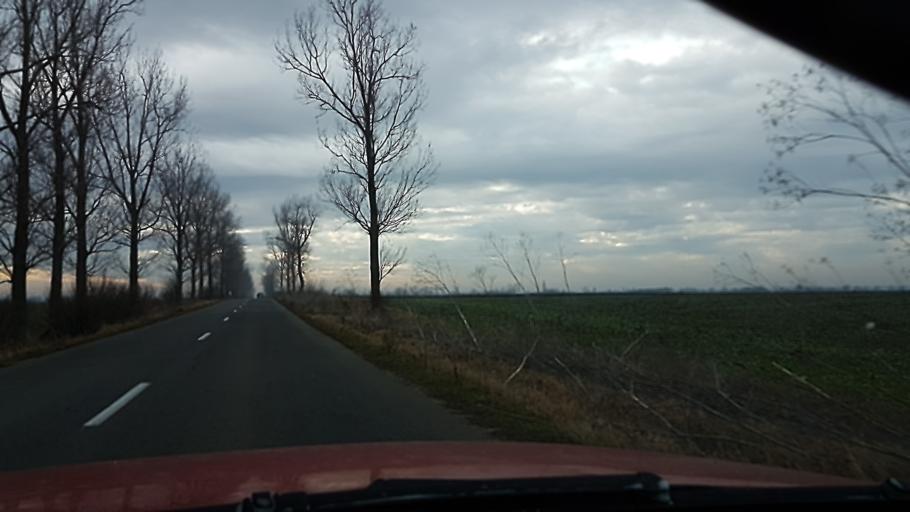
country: RO
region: Giurgiu
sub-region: Comuna Herasti
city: Herasti
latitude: 44.2287
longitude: 26.3608
